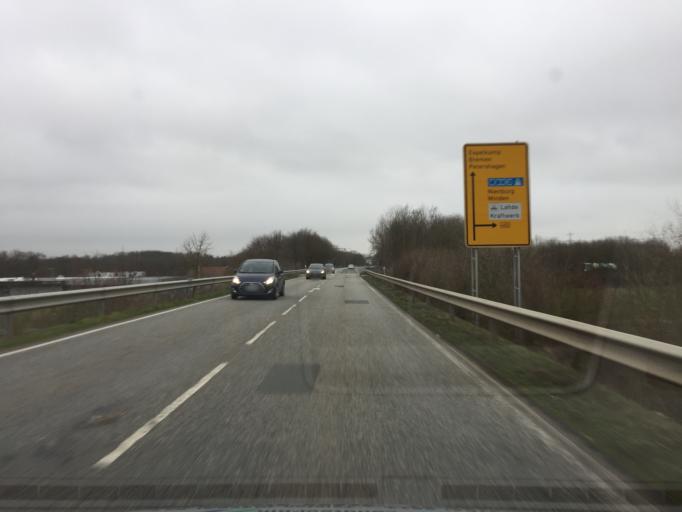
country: DE
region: North Rhine-Westphalia
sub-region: Regierungsbezirk Detmold
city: Petershagen
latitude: 52.3756
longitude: 9.0016
